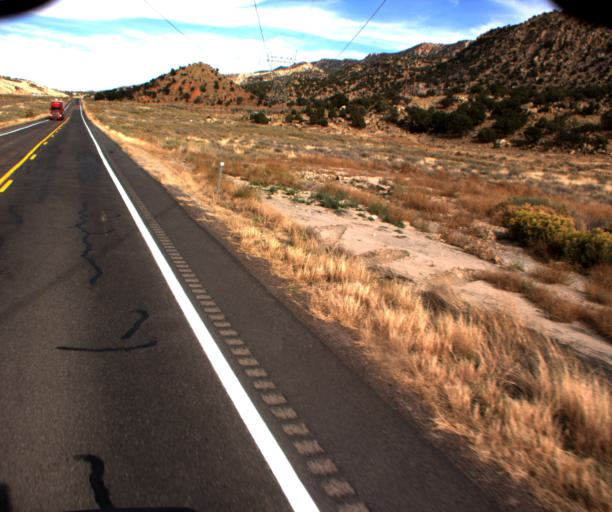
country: US
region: Arizona
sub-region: Navajo County
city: Kayenta
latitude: 36.6237
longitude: -110.4601
